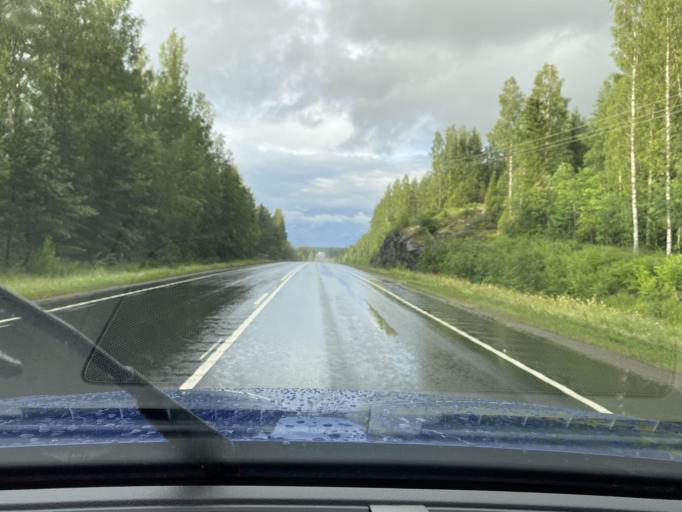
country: FI
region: Uusimaa
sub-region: Helsinki
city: Nurmijaervi
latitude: 60.4636
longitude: 24.8350
